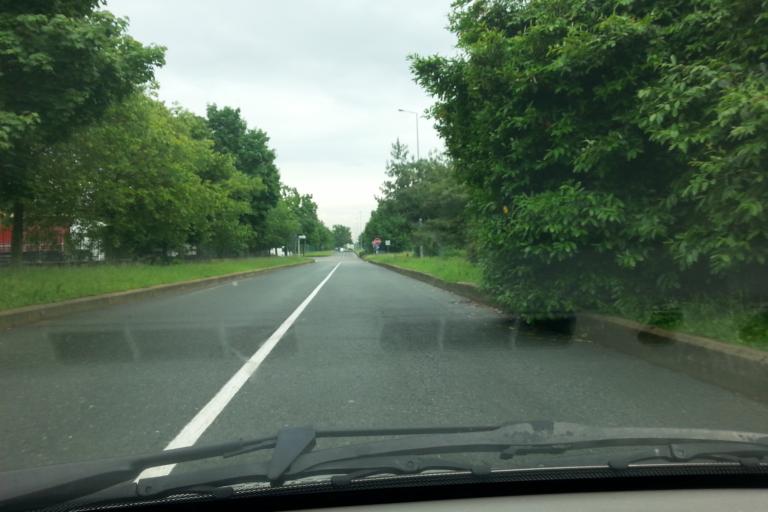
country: IT
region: Piedmont
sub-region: Provincia di Torino
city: Pasta
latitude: 45.0342
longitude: 7.5582
